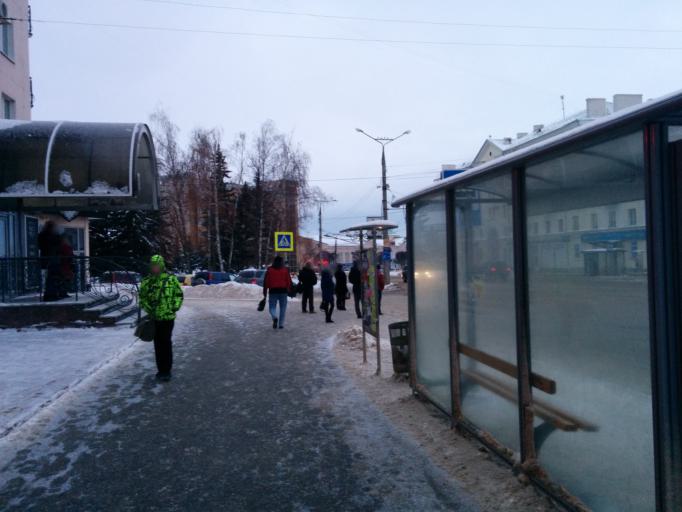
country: RU
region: Chuvashia
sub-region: Cheboksarskiy Rayon
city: Cheboksary
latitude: 56.1310
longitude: 47.2466
